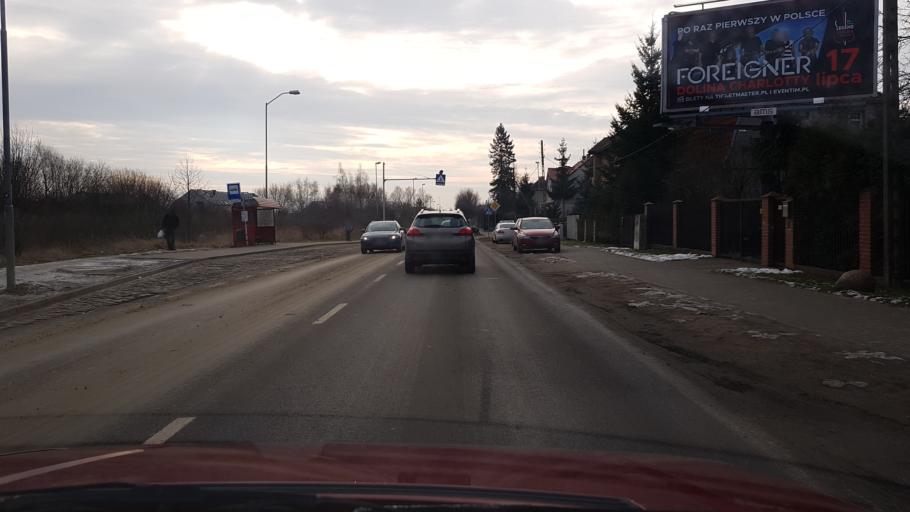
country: PL
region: West Pomeranian Voivodeship
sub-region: Powiat policki
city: Police
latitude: 53.4939
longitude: 14.5837
